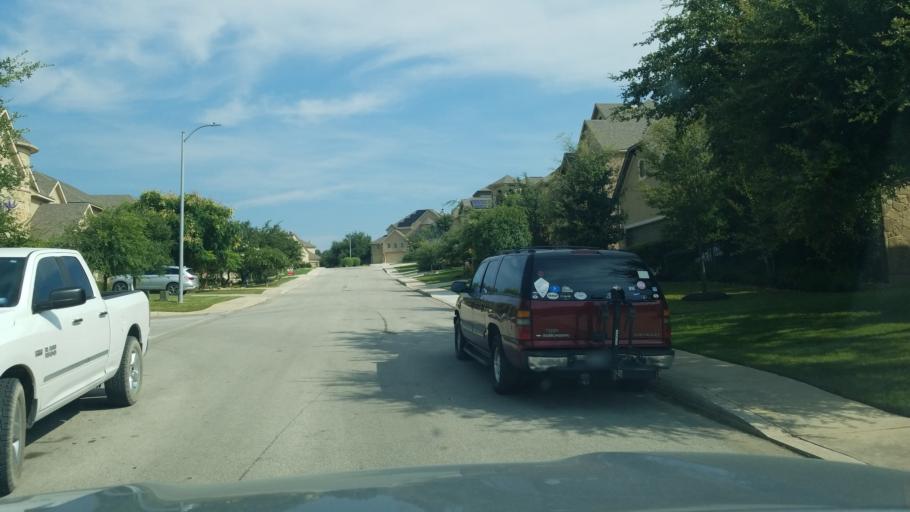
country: US
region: Texas
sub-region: Bexar County
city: Scenic Oaks
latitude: 29.7161
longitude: -98.6570
